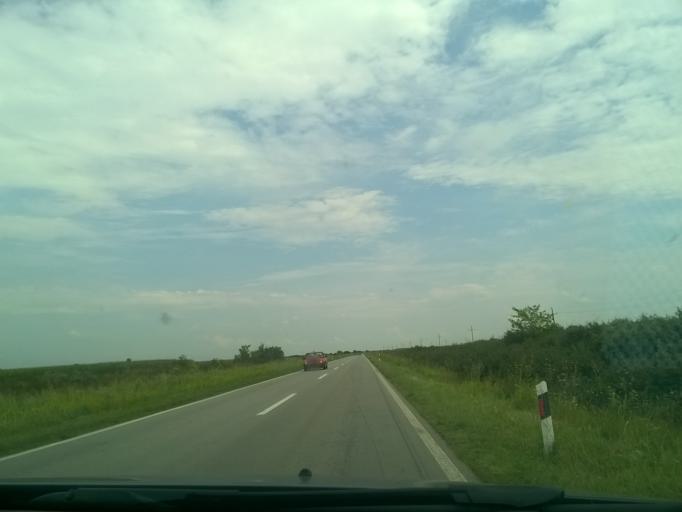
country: RS
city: Velika Greda
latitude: 45.2526
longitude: 21.0723
